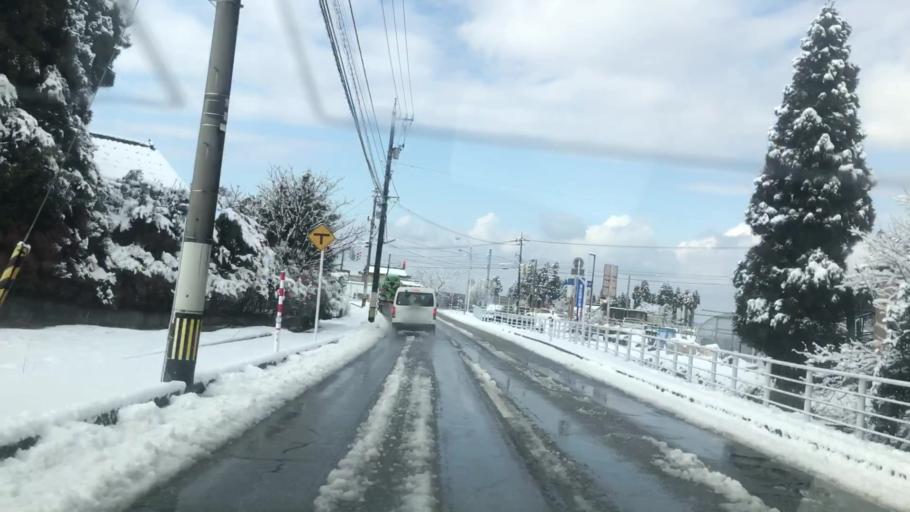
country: JP
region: Toyama
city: Toyama-shi
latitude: 36.6292
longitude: 137.2366
